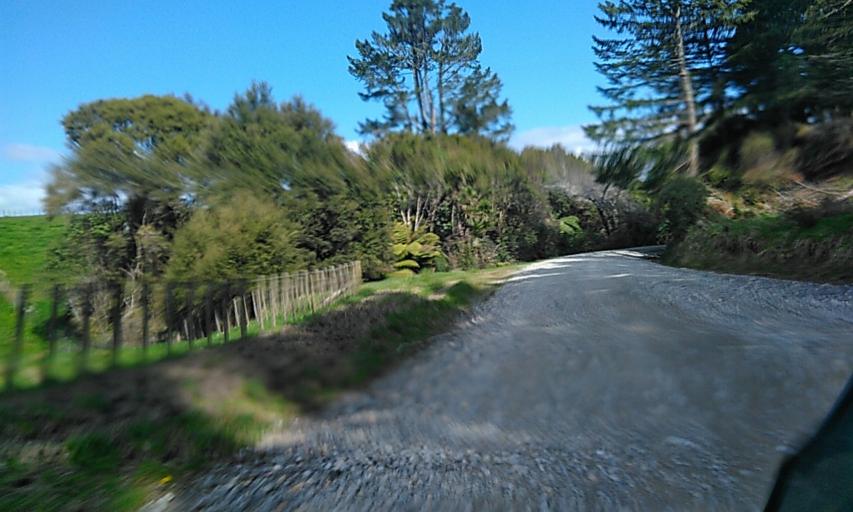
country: NZ
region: Gisborne
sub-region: Gisborne District
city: Gisborne
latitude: -38.2160
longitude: 178.0699
